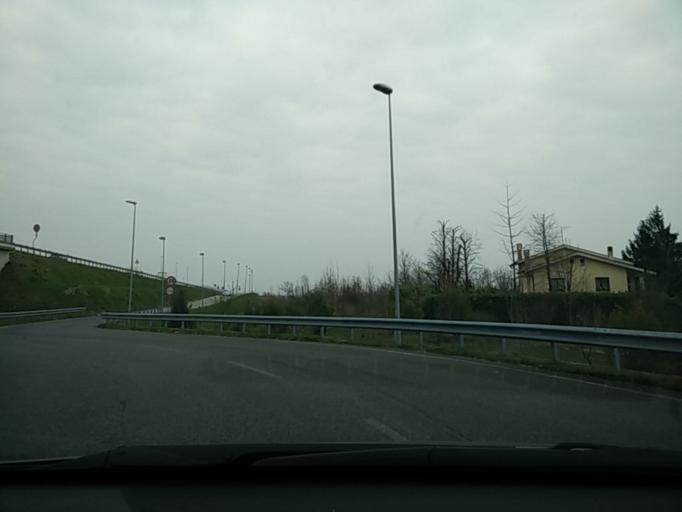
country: IT
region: Veneto
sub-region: Provincia di Venezia
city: San Dona di Piave
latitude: 45.6559
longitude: 12.5731
